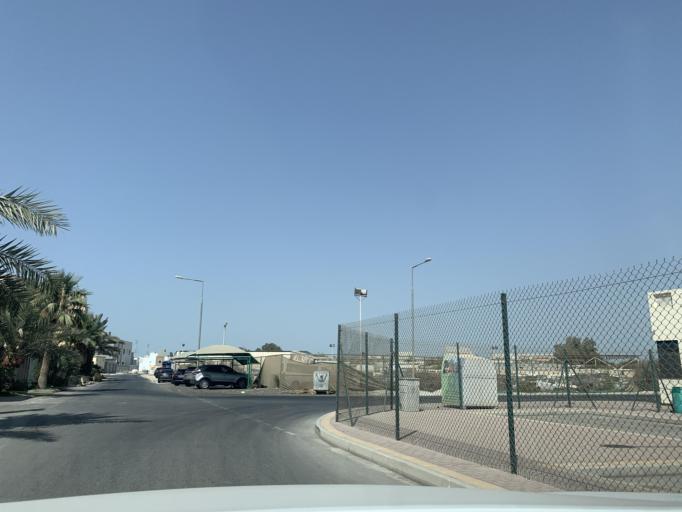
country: BH
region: Manama
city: Jidd Hafs
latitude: 26.2278
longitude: 50.4610
